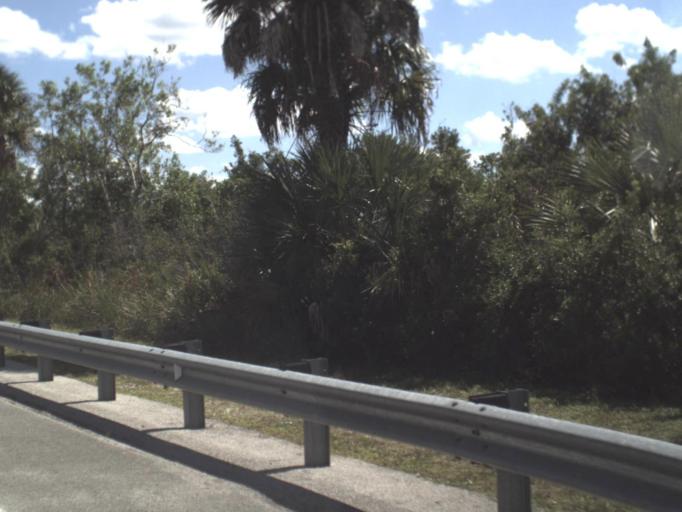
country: US
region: Florida
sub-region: Collier County
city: Marco
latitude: 25.9691
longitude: -81.5394
